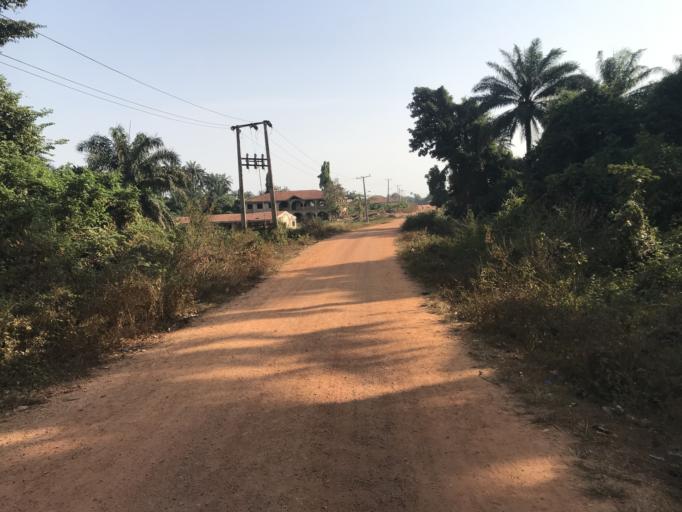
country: NG
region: Osun
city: Awo
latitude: 7.7560
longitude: 4.3170
